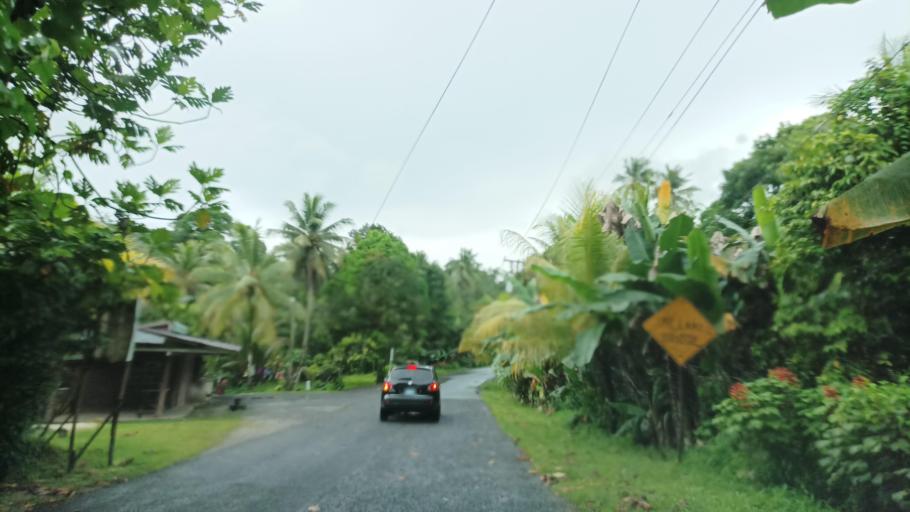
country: FM
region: Pohnpei
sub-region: Sokehs Municipality
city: Palikir - National Government Center
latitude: 6.8785
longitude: 158.1602
